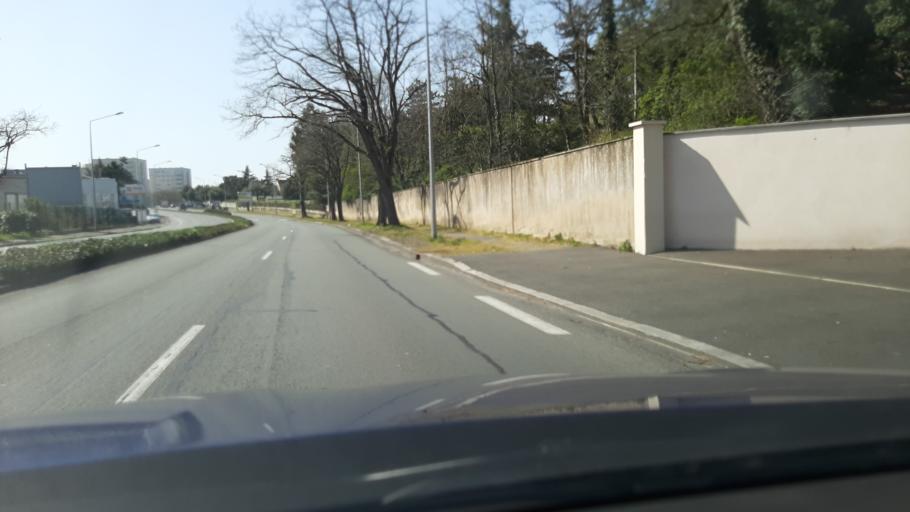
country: FR
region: Pays de la Loire
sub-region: Departement de Maine-et-Loire
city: Angers
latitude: 47.4575
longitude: -0.5266
